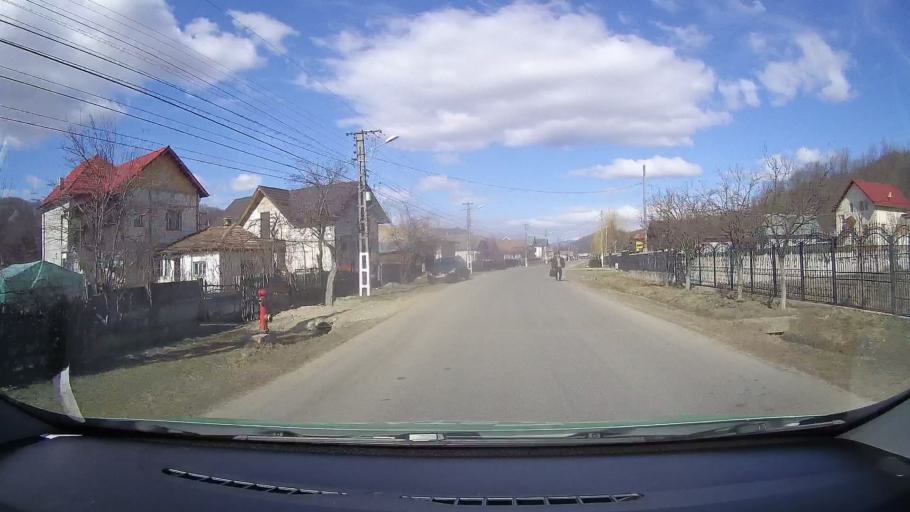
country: RO
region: Dambovita
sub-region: Comuna Vulcana-Pandele
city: Gura Vulcanei
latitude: 45.0315
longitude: 25.3941
